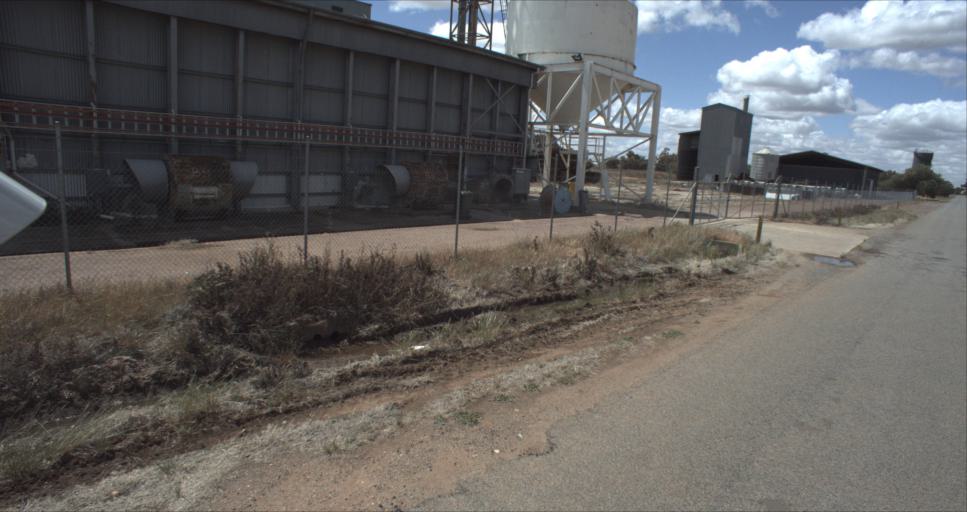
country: AU
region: New South Wales
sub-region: Murrumbidgee Shire
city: Darlington Point
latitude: -34.5153
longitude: 146.1782
